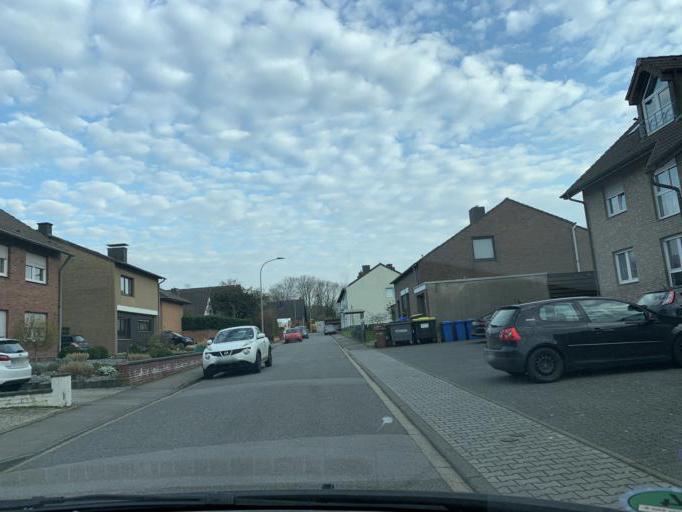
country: DE
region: North Rhine-Westphalia
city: Julich
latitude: 50.9199
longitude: 6.4135
